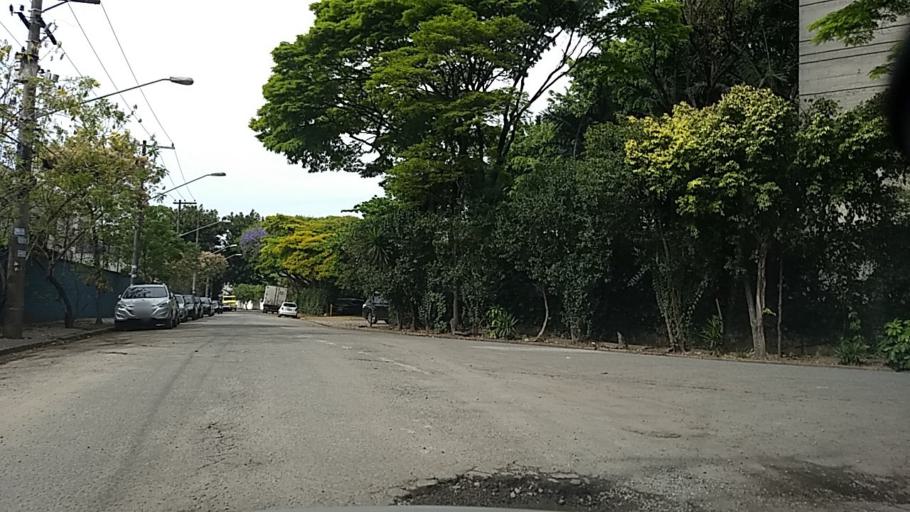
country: BR
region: Sao Paulo
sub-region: Guarulhos
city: Guarulhos
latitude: -23.4993
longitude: -46.5651
